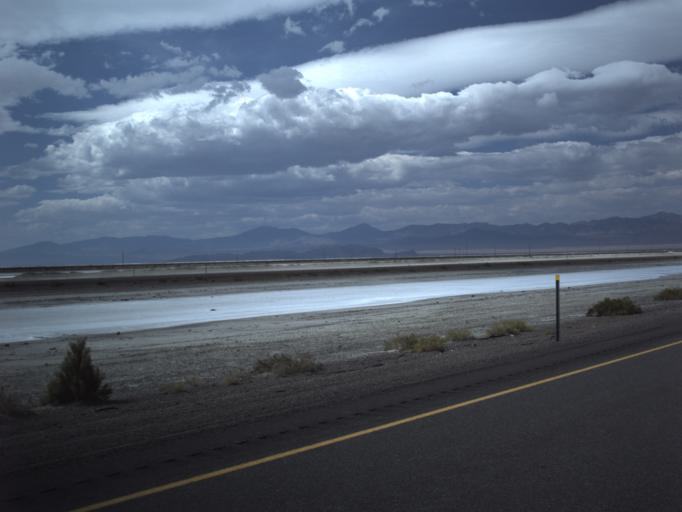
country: US
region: Utah
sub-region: Tooele County
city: Wendover
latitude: 40.7409
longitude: -113.9255
